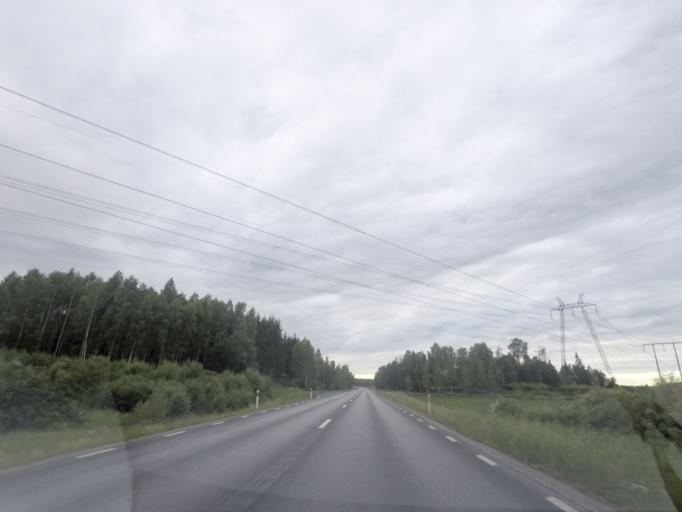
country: SE
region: OErebro
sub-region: Lindesbergs Kommun
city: Lindesberg
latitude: 59.5418
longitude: 15.2488
